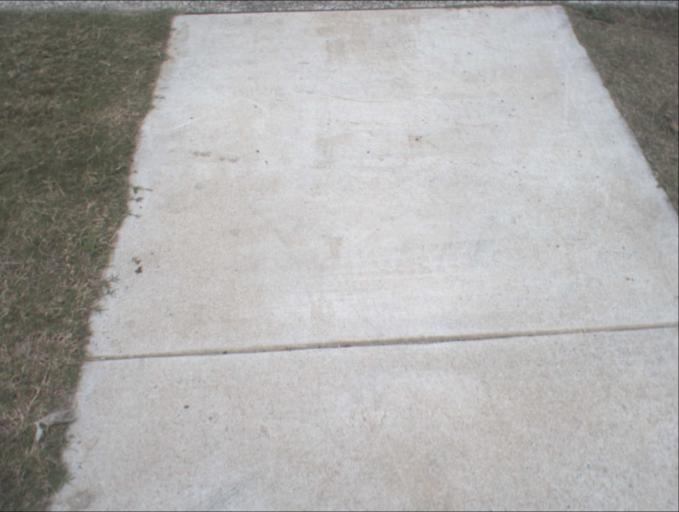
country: AU
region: Queensland
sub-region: Logan
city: Chambers Flat
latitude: -27.7977
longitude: 153.1045
